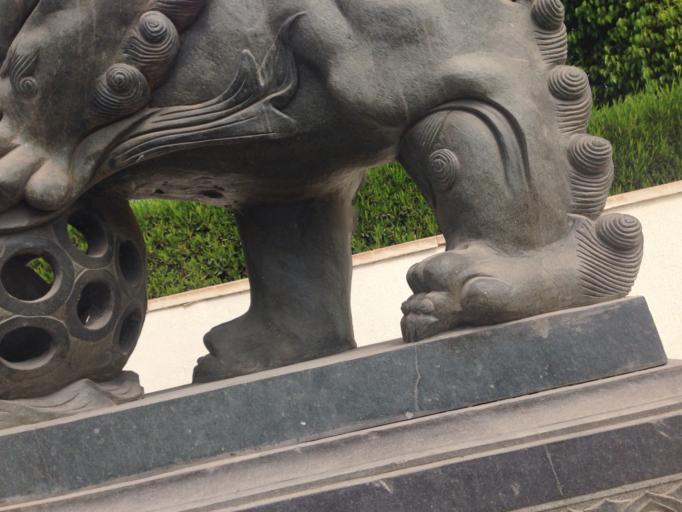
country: EG
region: Muhafazat al Qalyubiyah
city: Al Khankah
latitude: 30.0721
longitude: 31.4331
